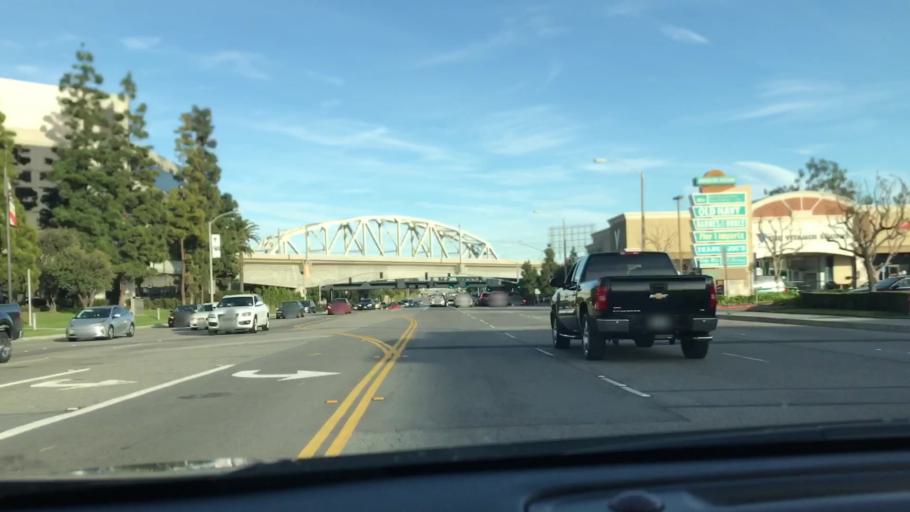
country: US
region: California
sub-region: Los Angeles County
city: Del Aire
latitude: 33.9019
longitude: -118.3810
